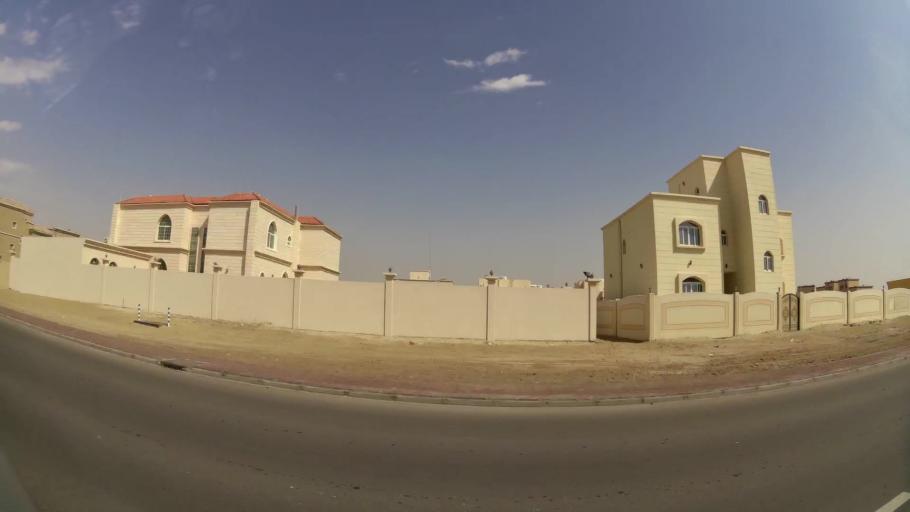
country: AE
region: Abu Dhabi
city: Abu Dhabi
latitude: 24.3189
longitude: 54.5621
